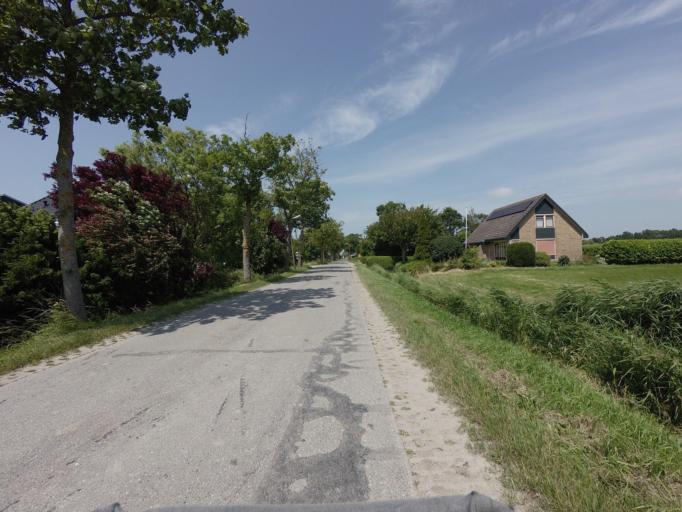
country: NL
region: North Holland
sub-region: Gemeente Opmeer
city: Opmeer
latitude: 52.6584
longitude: 4.9350
